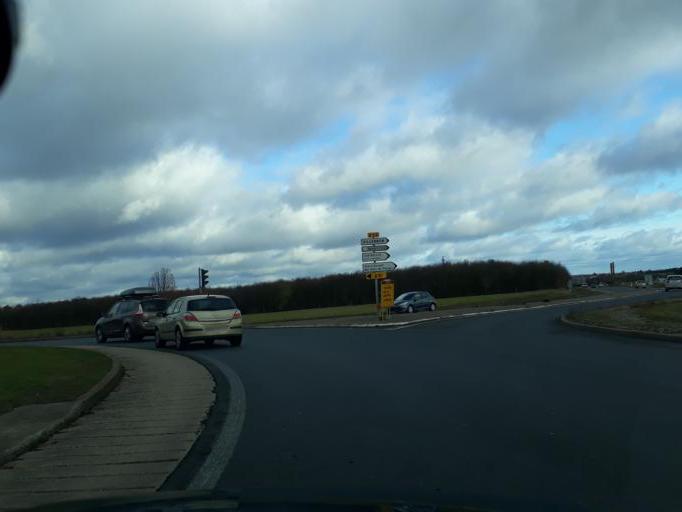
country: FR
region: Centre
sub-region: Departement du Loir-et-Cher
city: La Chaussee-Saint-Victor
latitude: 47.6173
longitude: 1.3476
